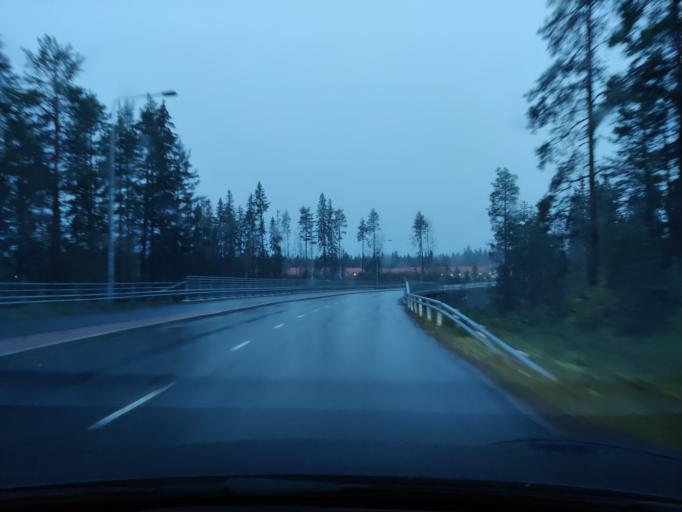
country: FI
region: Northern Savo
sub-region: Kuopio
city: Kuopio
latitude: 62.8282
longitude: 27.7014
